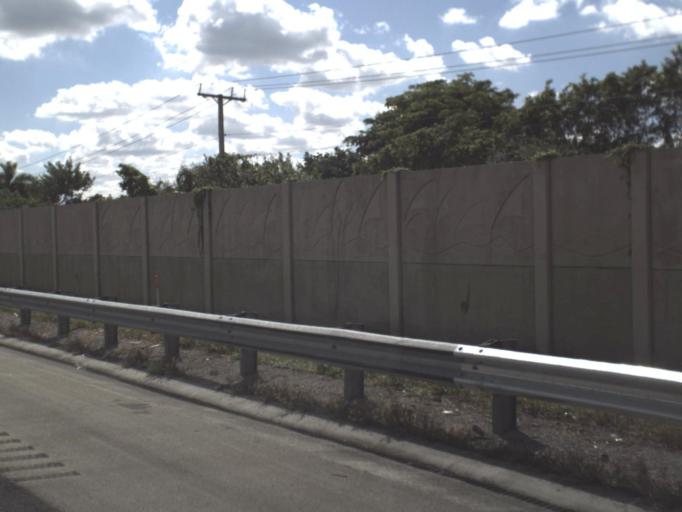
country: US
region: Florida
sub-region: Broward County
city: Broadview Park
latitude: 26.1114
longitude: -80.2187
